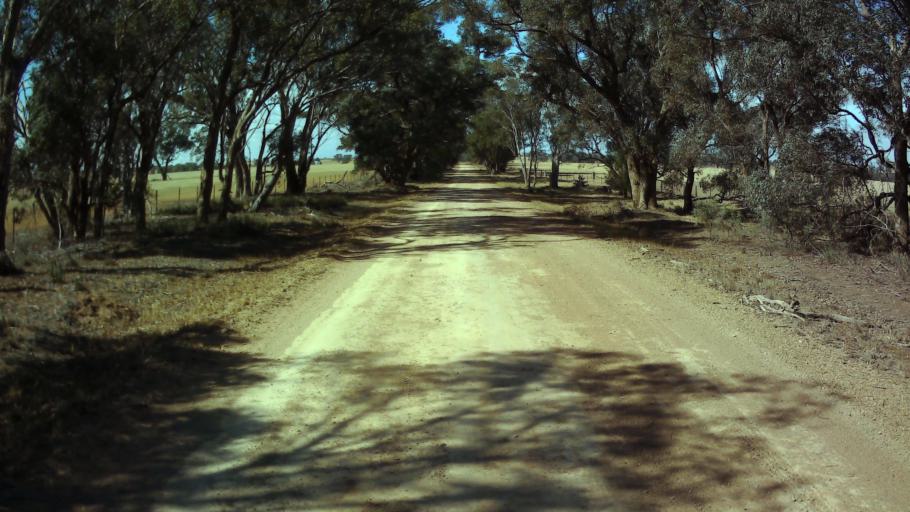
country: AU
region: New South Wales
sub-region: Weddin
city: Grenfell
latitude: -34.0514
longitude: 148.3138
